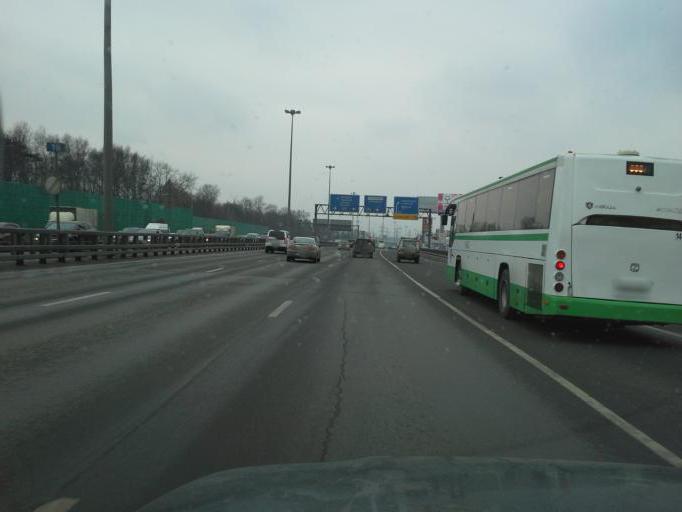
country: RU
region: Moskovskaya
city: Mosrentgen
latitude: 55.6349
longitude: 37.4507
